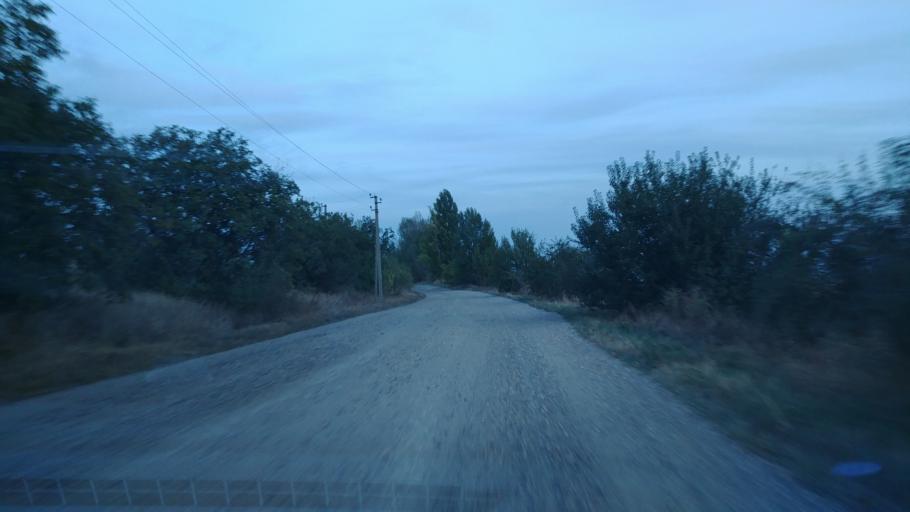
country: MD
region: Rezina
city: Saharna
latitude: 47.6770
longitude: 28.9263
